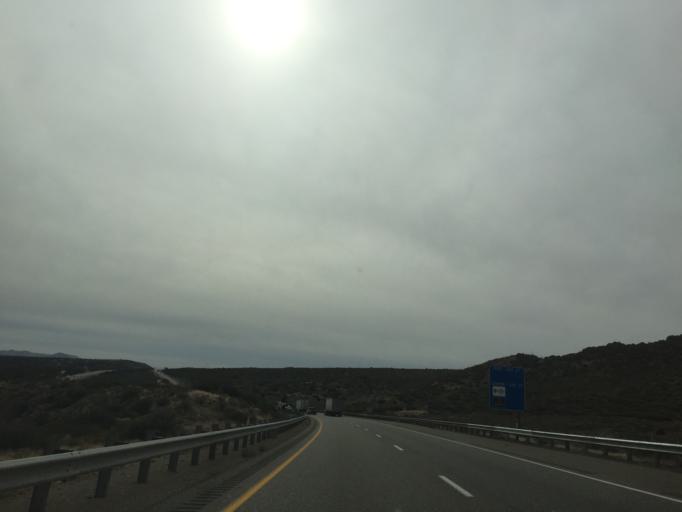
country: US
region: Utah
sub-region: Washington County
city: Toquerville
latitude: 37.3083
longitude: -113.2977
